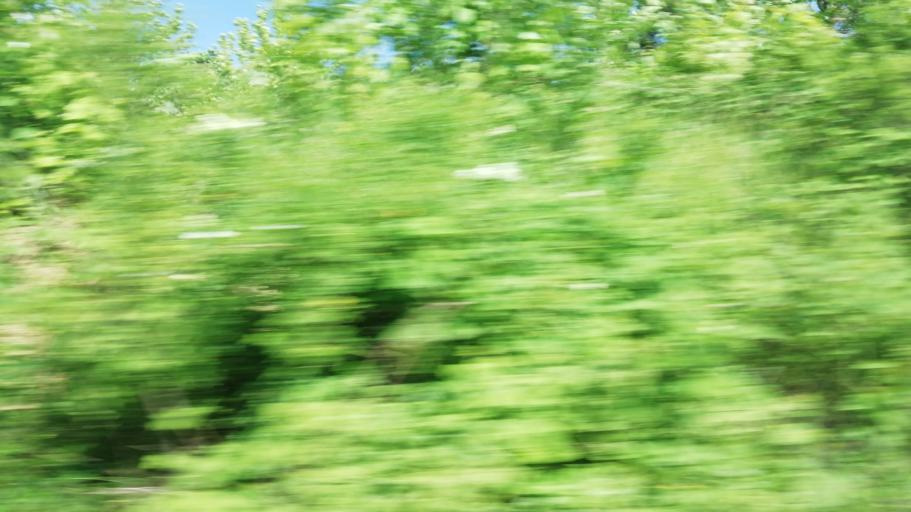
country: TR
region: Karabuk
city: Karabuk
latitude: 41.1261
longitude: 32.5755
